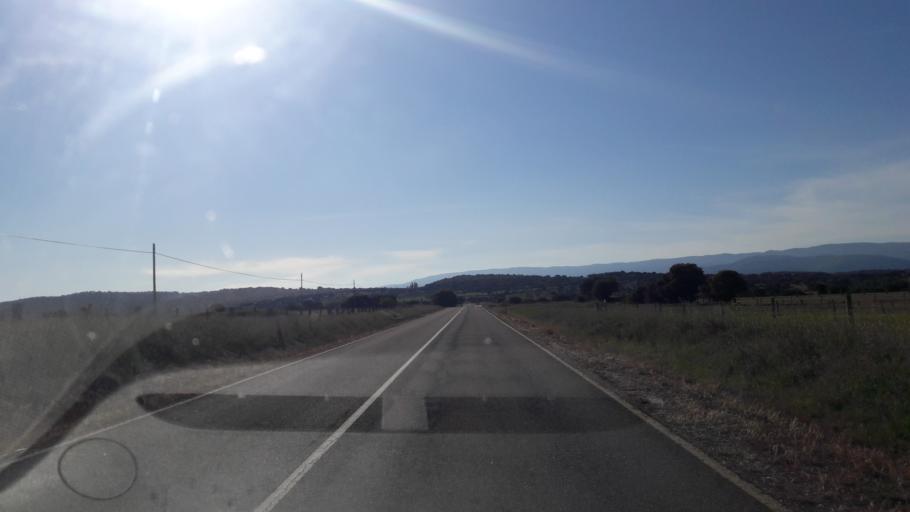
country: ES
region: Castille and Leon
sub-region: Provincia de Salamanca
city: Puente del Congosto
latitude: 40.5257
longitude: -5.5063
